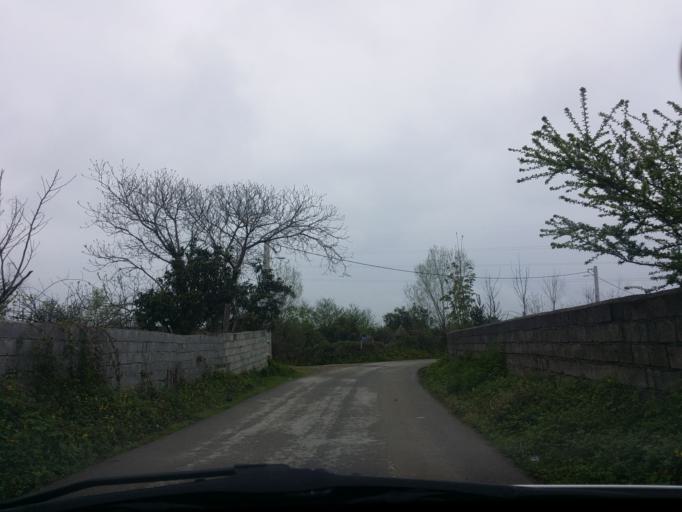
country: IR
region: Mazandaran
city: Chalus
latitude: 36.6733
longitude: 51.3790
